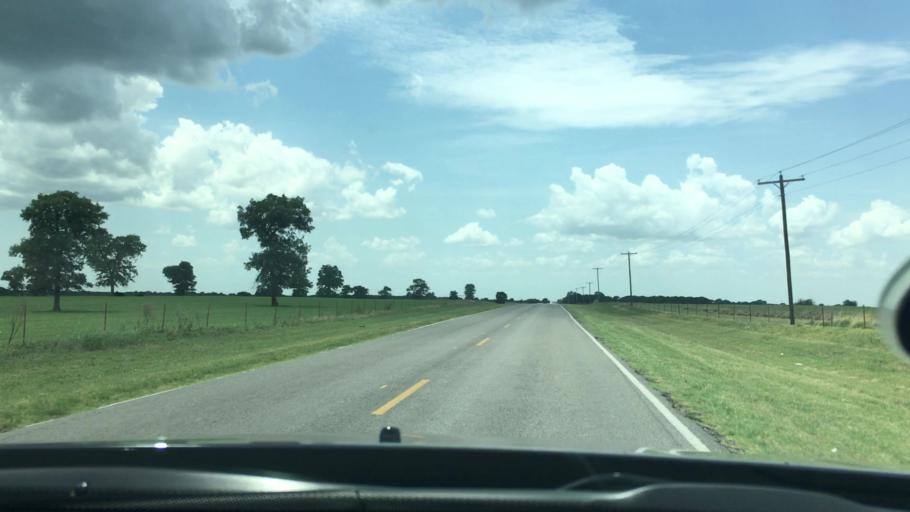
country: US
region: Oklahoma
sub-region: Carter County
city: Wilson
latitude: 33.9403
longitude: -97.3894
